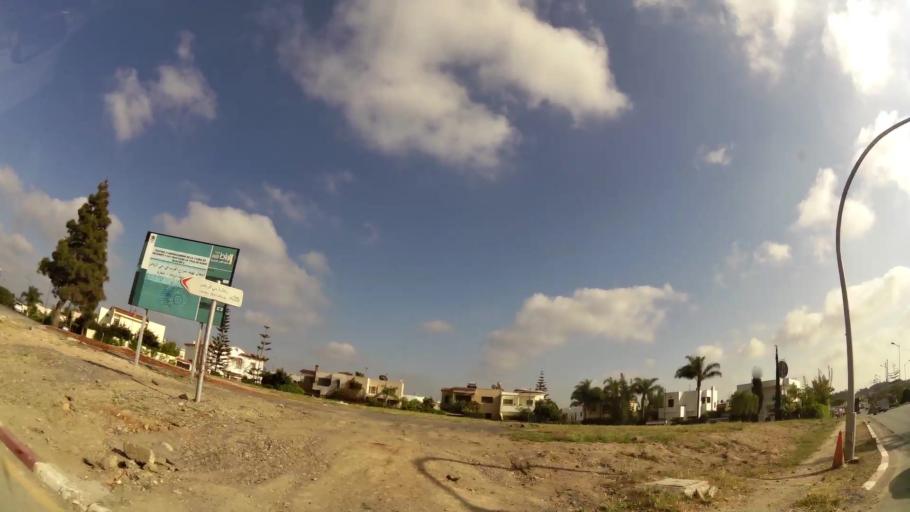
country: MA
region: Rabat-Sale-Zemmour-Zaer
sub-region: Skhirate-Temara
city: Temara
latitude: 33.9498
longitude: -6.8683
